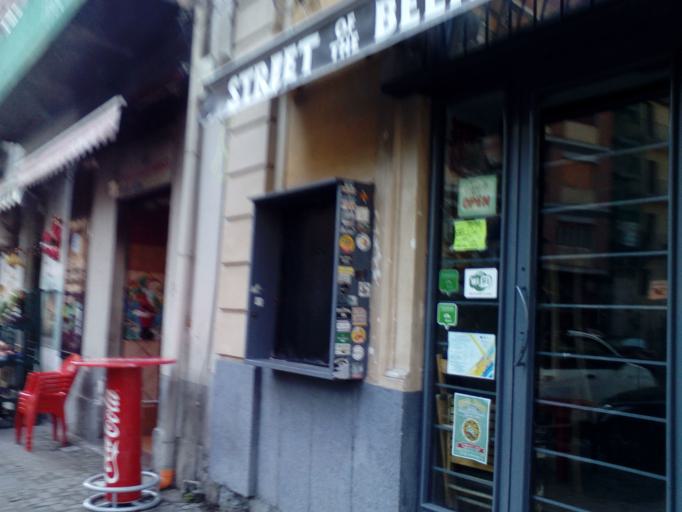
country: IT
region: Sicily
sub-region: Catania
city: Canalicchio
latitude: 37.5154
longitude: 15.0872
